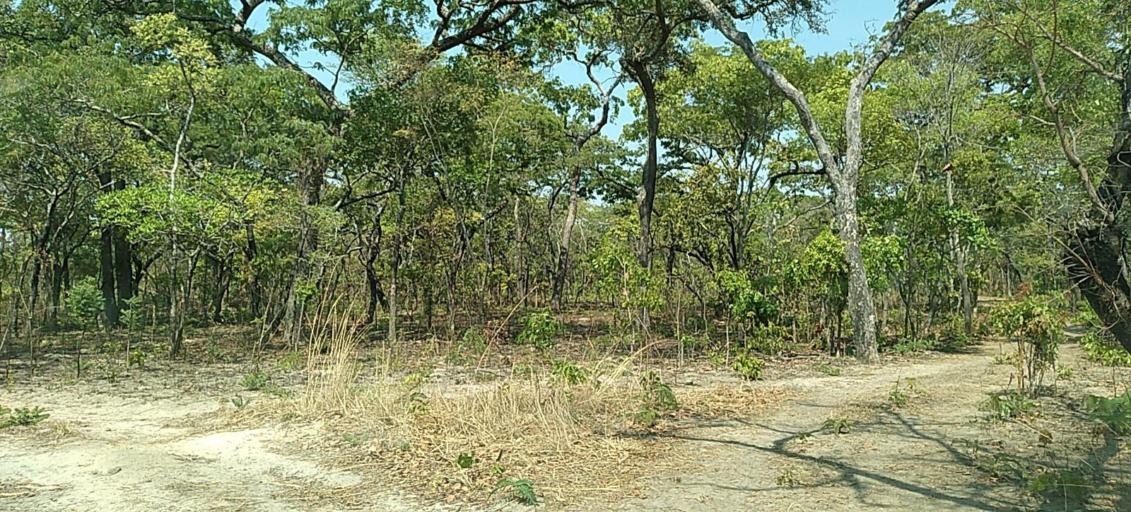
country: ZM
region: Copperbelt
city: Mpongwe
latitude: -13.7852
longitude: 28.0991
